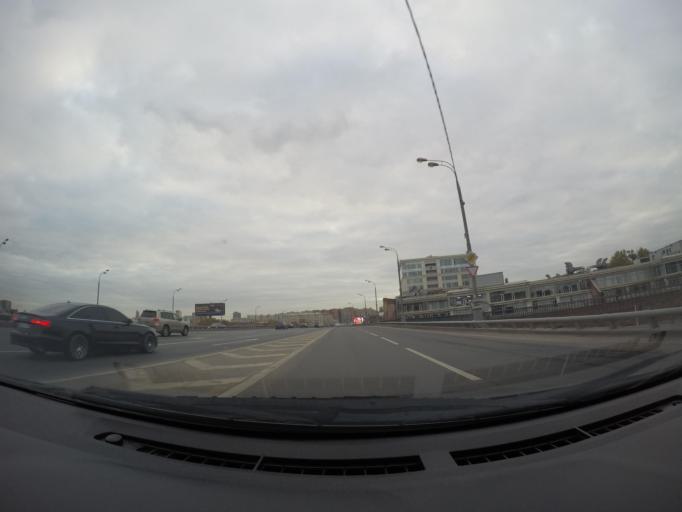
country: RU
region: Moscow
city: Sokol'niki
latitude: 55.7798
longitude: 37.6726
